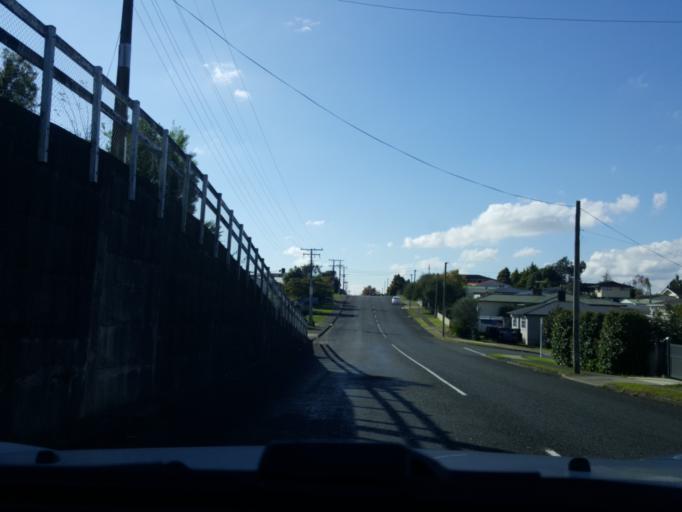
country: NZ
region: Waikato
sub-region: Waikato District
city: Ngaruawahia
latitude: -37.5450
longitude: 175.1691
